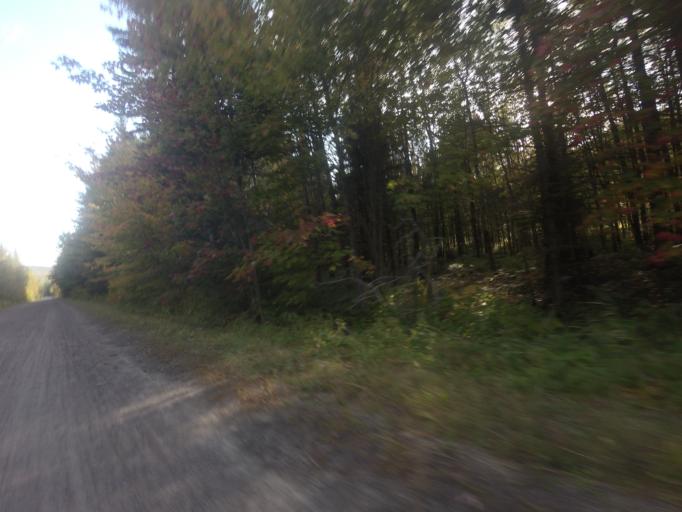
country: CA
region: Quebec
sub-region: Laurentides
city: Sainte-Adele
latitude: 45.9591
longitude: -74.1037
